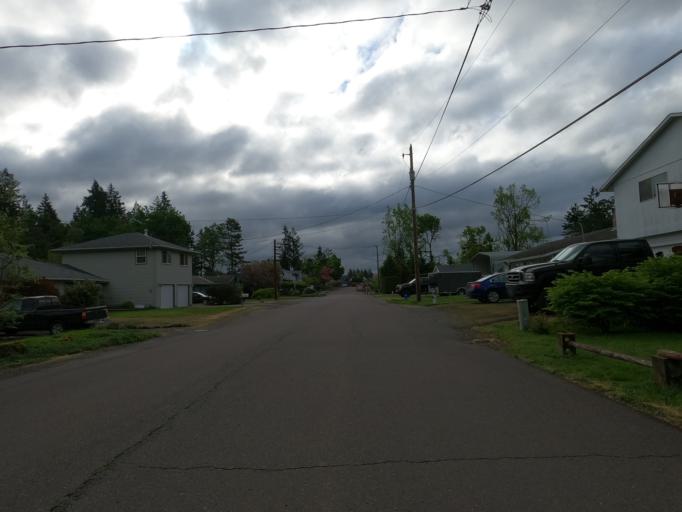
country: US
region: Oregon
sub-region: Clackamas County
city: Oatfield
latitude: 45.3998
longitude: -122.5902
